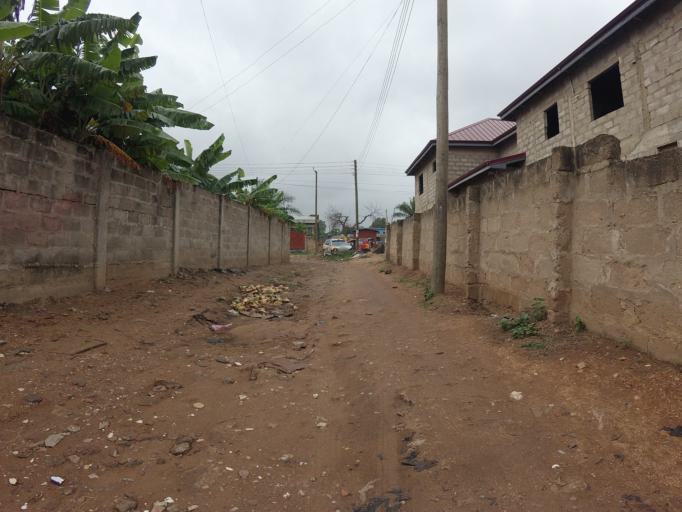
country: GH
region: Greater Accra
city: Dome
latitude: 5.6311
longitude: -0.2318
